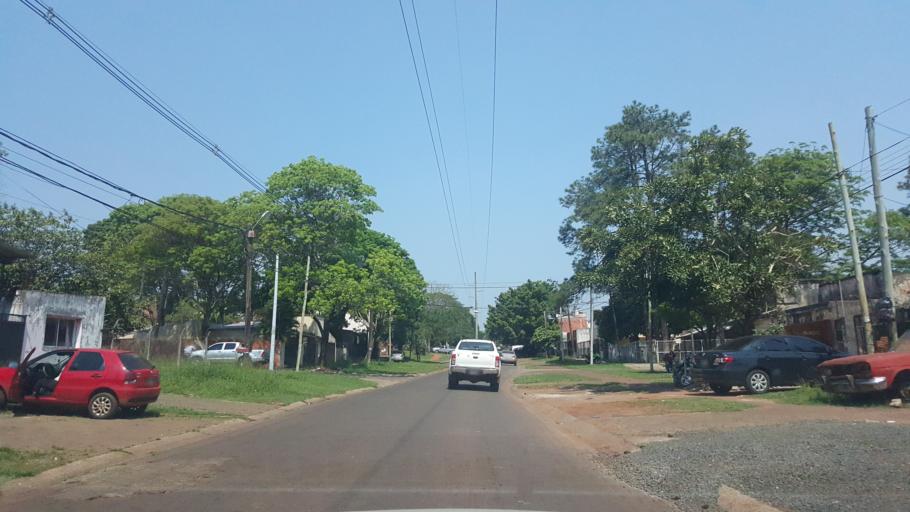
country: AR
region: Misiones
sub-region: Departamento de Capital
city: Posadas
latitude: -27.3731
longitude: -55.9136
